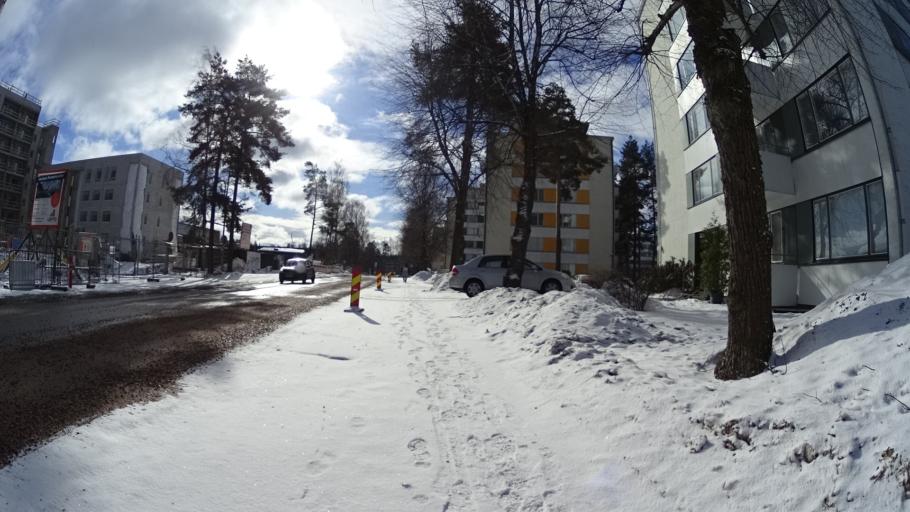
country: FI
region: Uusimaa
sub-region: Helsinki
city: Teekkarikylae
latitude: 60.2657
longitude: 24.8722
